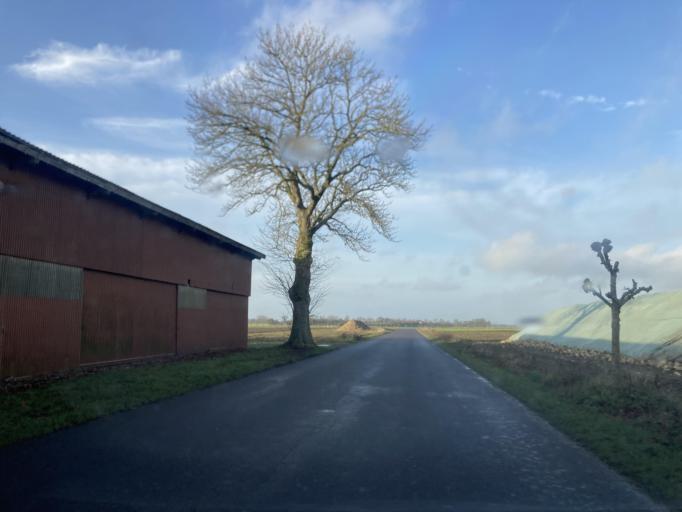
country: DK
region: Zealand
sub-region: Lolland Kommune
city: Rodby
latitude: 54.6898
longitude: 11.3738
